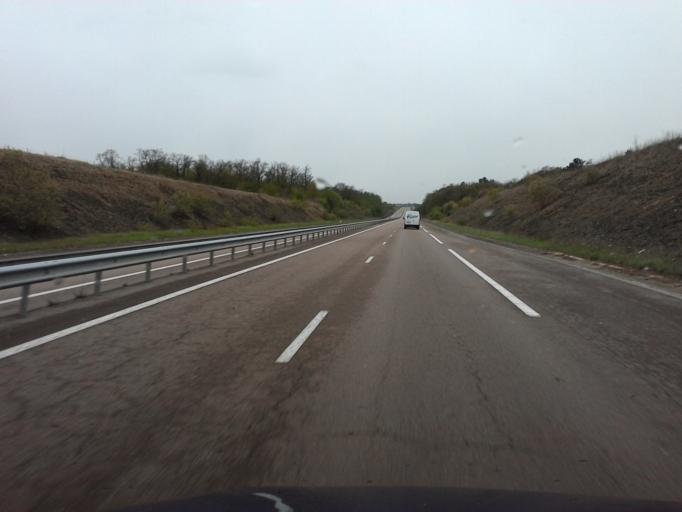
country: FR
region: Champagne-Ardenne
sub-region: Departement de la Haute-Marne
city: Chaumont
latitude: 48.1495
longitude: 5.1176
